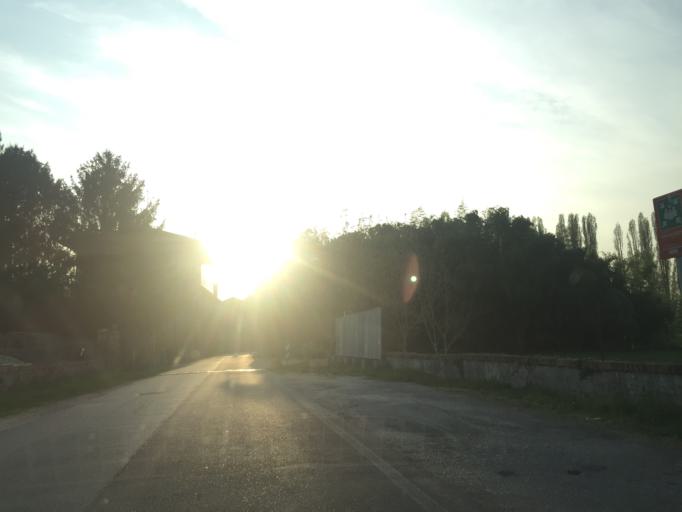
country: IT
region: Friuli Venezia Giulia
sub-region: Provincia di Pordenone
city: Cavolano-Schiavoi
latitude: 45.9365
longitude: 12.4757
